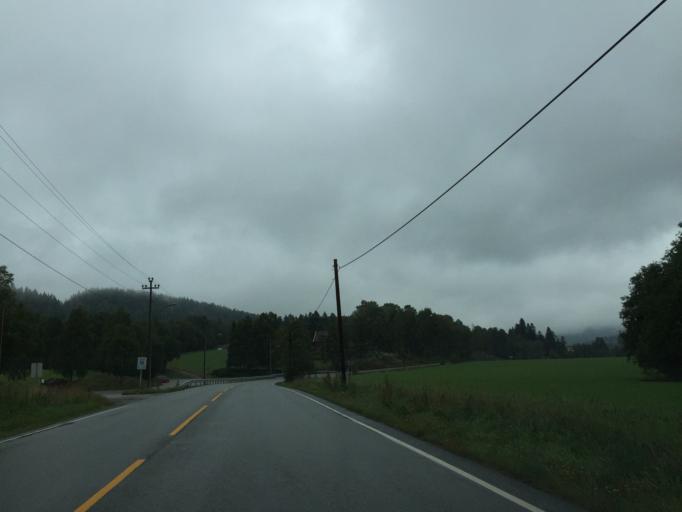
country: NO
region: Akershus
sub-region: Baerum
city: Lysaker
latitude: 59.9868
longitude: 10.6210
